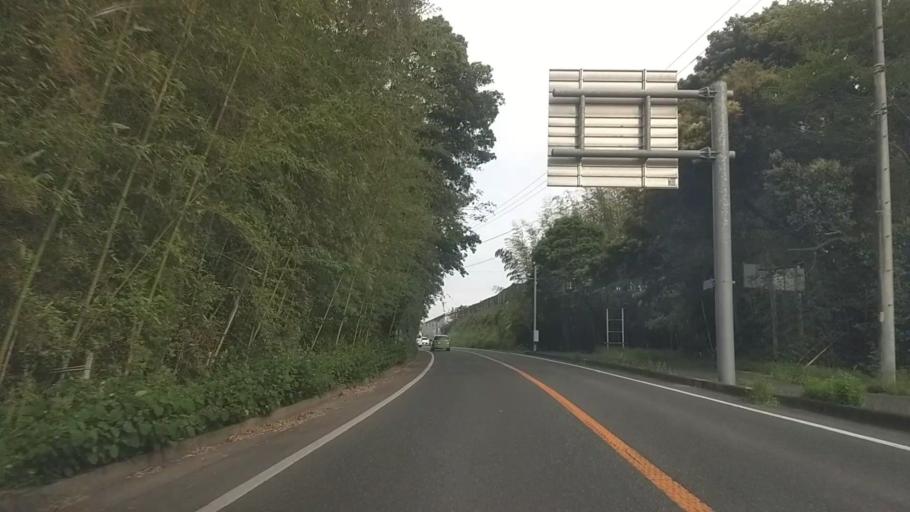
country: JP
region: Shizuoka
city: Hamamatsu
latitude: 34.7604
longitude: 137.6636
